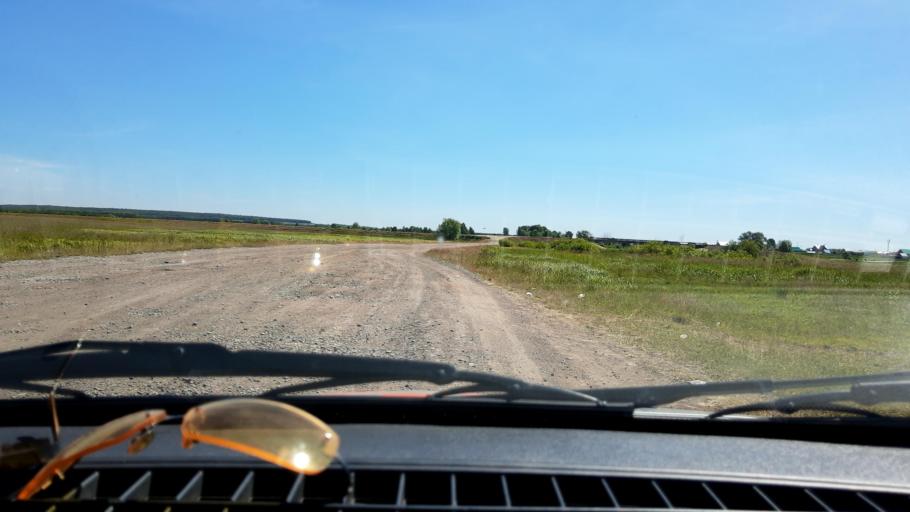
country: RU
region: Bashkortostan
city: Mikhaylovka
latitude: 54.9675
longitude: 55.7993
